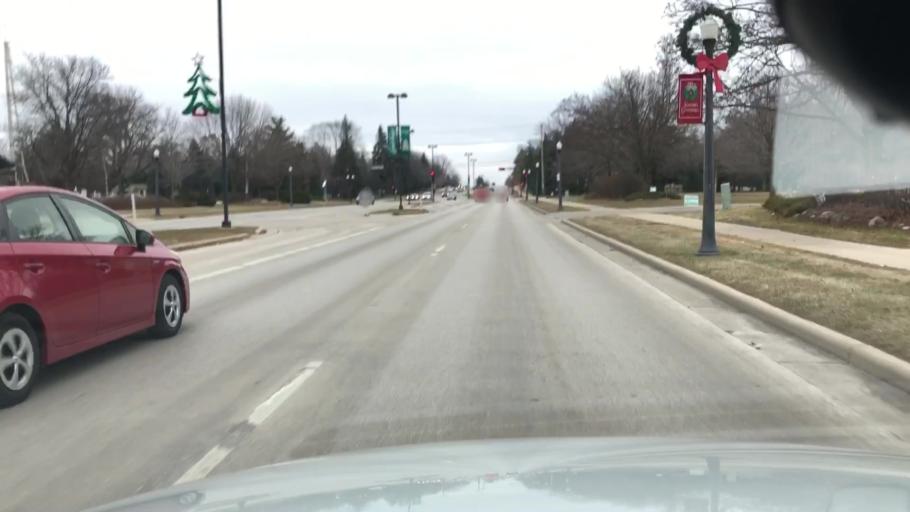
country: US
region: Wisconsin
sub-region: Waukesha County
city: Brookfield
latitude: 43.0550
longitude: -88.1264
